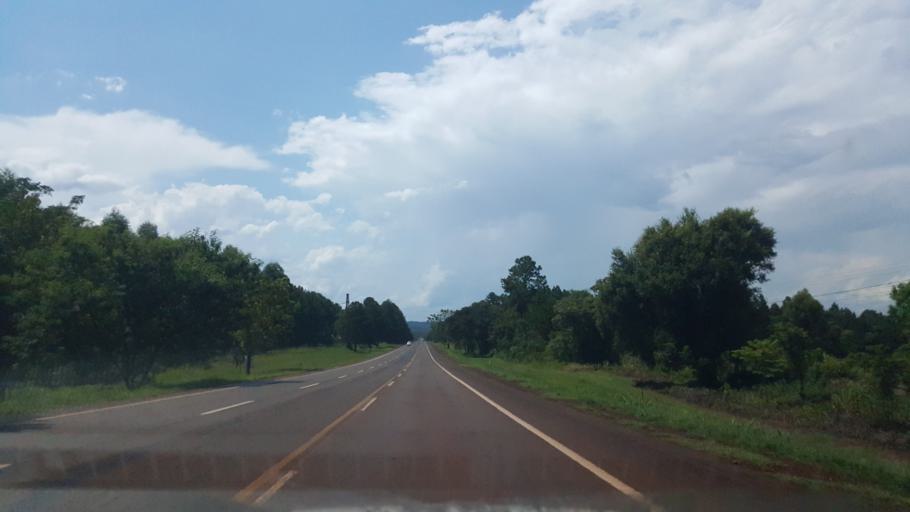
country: AR
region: Misiones
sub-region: Departamento de Eldorado
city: Eldorado
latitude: -26.3843
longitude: -54.6285
